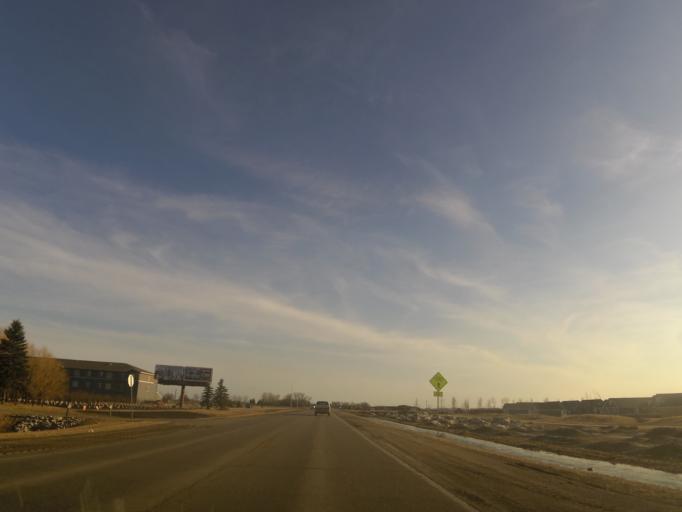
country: US
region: North Dakota
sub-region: Grand Forks County
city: Grand Forks
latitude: 47.8699
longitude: -97.0454
